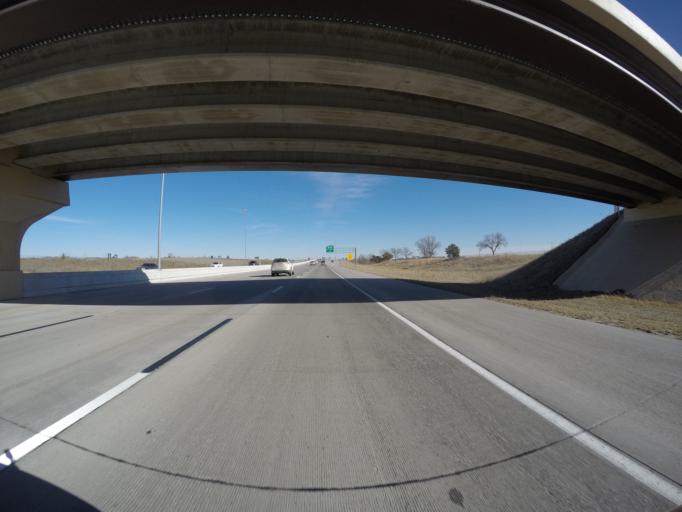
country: US
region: Nebraska
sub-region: Lancaster County
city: Lincoln
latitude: 40.8185
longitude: -96.7966
